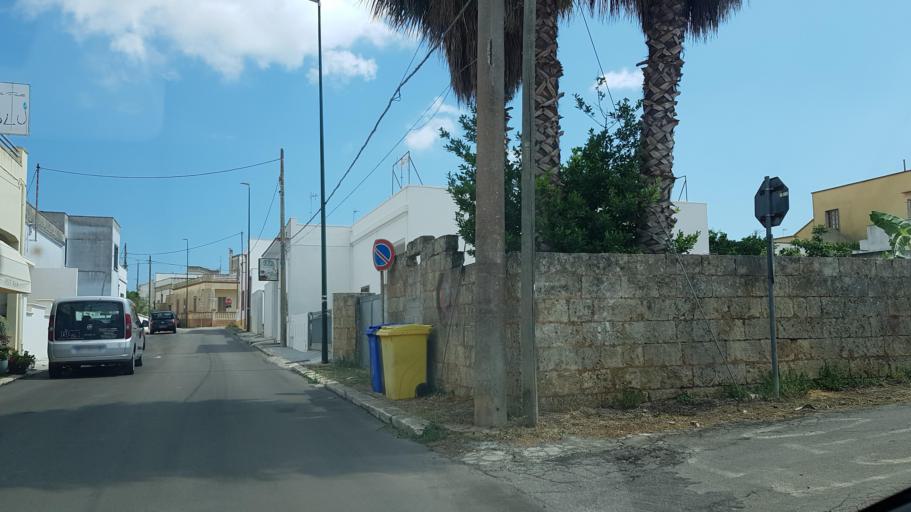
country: IT
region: Apulia
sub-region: Provincia di Lecce
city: Castrignano del Capo
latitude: 39.8332
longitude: 18.3528
